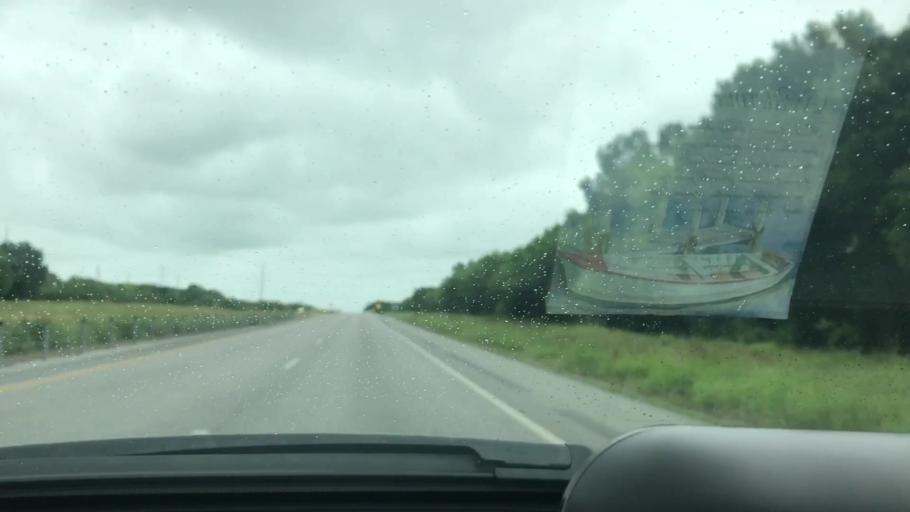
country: US
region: Oklahoma
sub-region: Coal County
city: Coalgate
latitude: 34.6202
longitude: -95.9649
